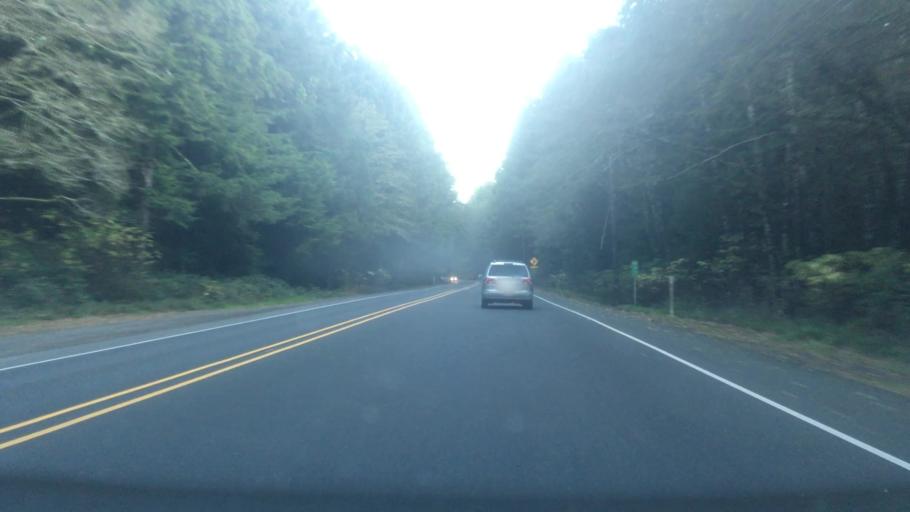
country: US
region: Oregon
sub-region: Clatsop County
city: Cannon Beach
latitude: 45.7851
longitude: -123.9582
